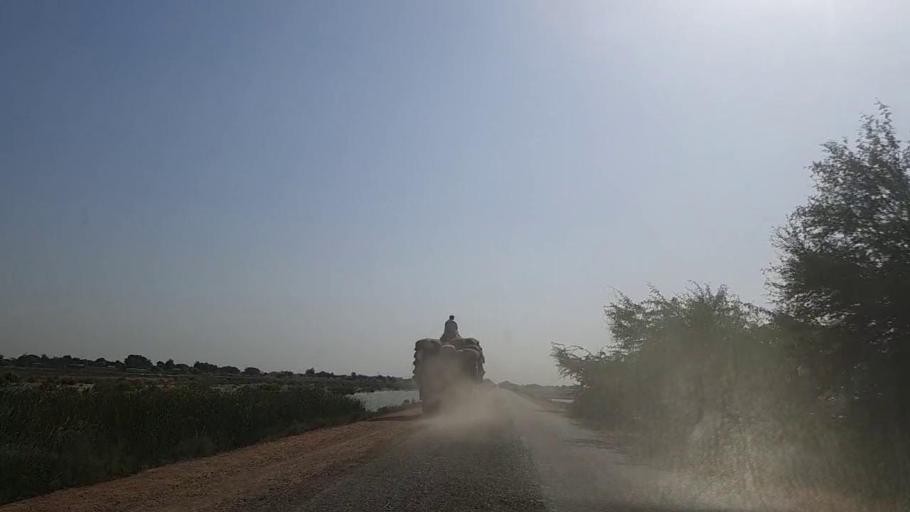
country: PK
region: Sindh
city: Mirpur Batoro
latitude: 24.5810
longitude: 68.2894
